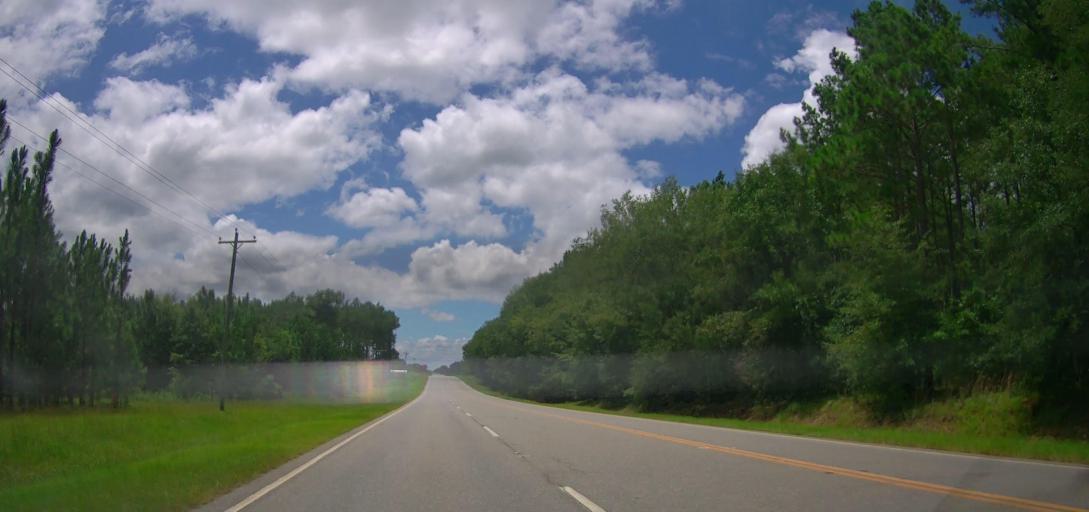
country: US
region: Georgia
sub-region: Turner County
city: Ashburn
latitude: 31.7218
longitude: -83.5239
